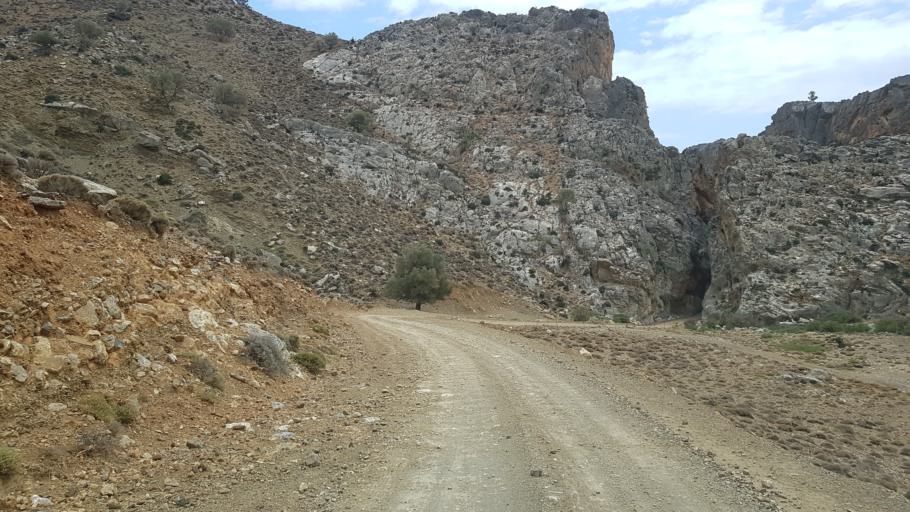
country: GR
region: Crete
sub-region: Nomos Irakleiou
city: Agioi Deka
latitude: 34.9444
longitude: 24.9855
